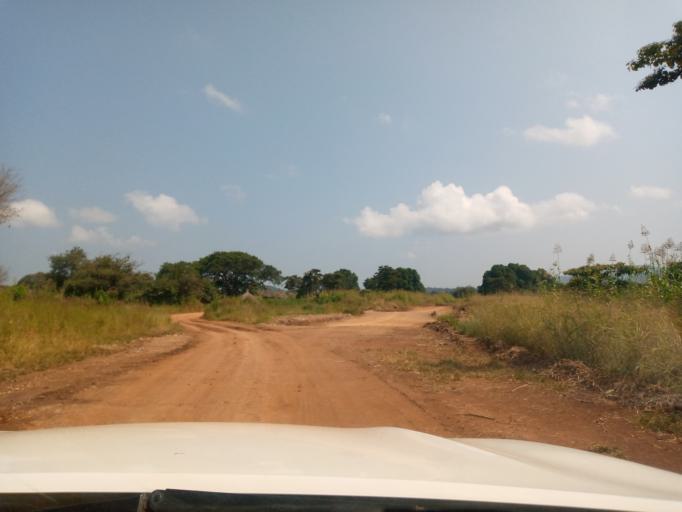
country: ET
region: Oromiya
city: Mendi
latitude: 10.2068
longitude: 35.0763
